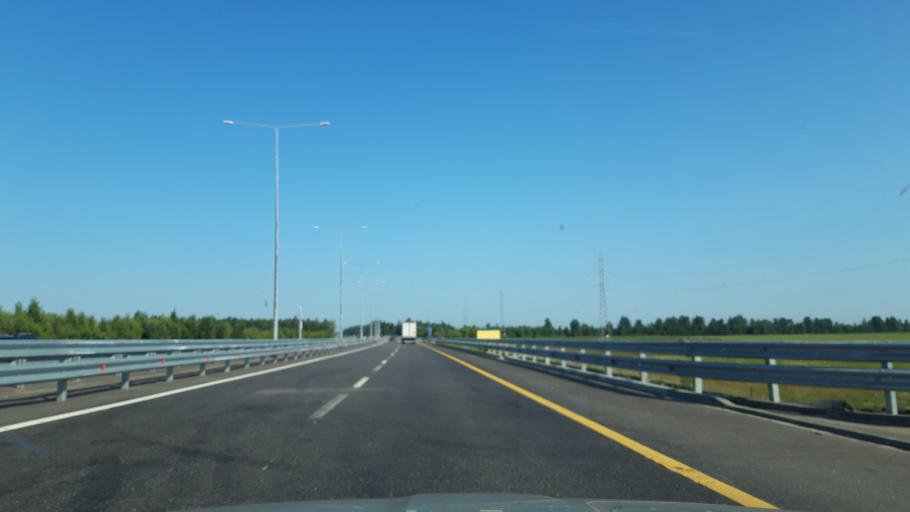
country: RU
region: Tverskaya
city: Zavidovo
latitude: 56.4947
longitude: 36.5293
